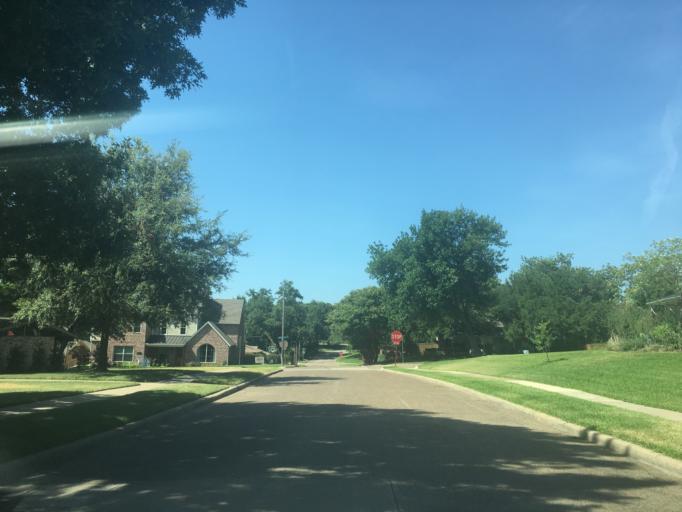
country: US
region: Texas
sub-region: Dallas County
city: Richardson
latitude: 32.8720
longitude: -96.7205
